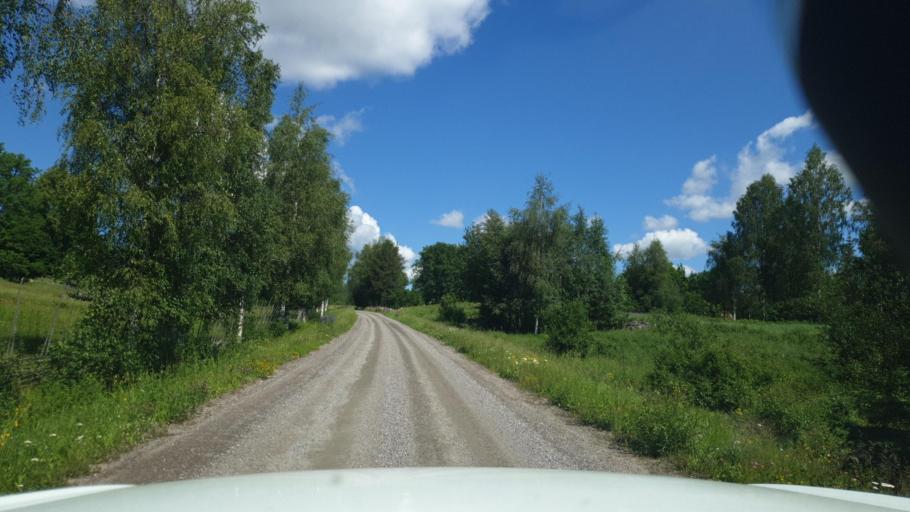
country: SE
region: Vaermland
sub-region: Eda Kommun
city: Charlottenberg
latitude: 59.9940
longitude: 12.5074
